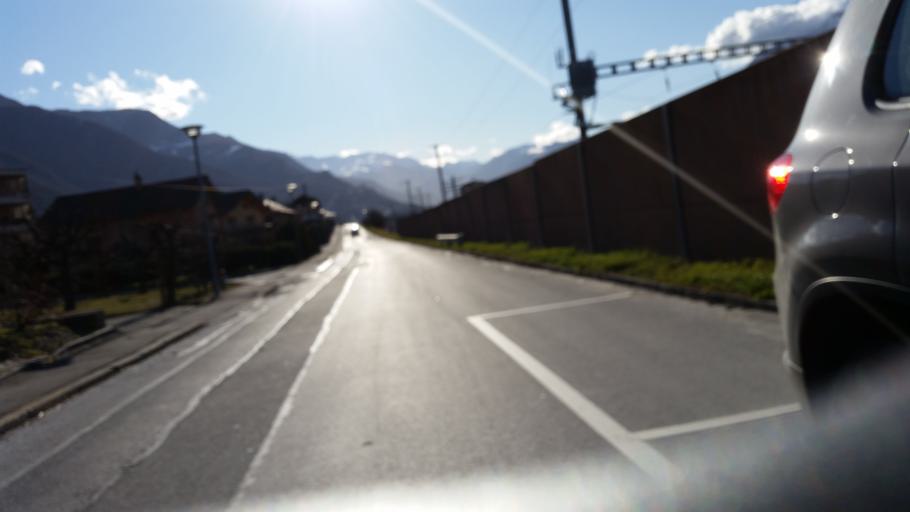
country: CH
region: Valais
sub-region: Martigny District
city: Riddes
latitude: 46.1761
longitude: 7.2228
